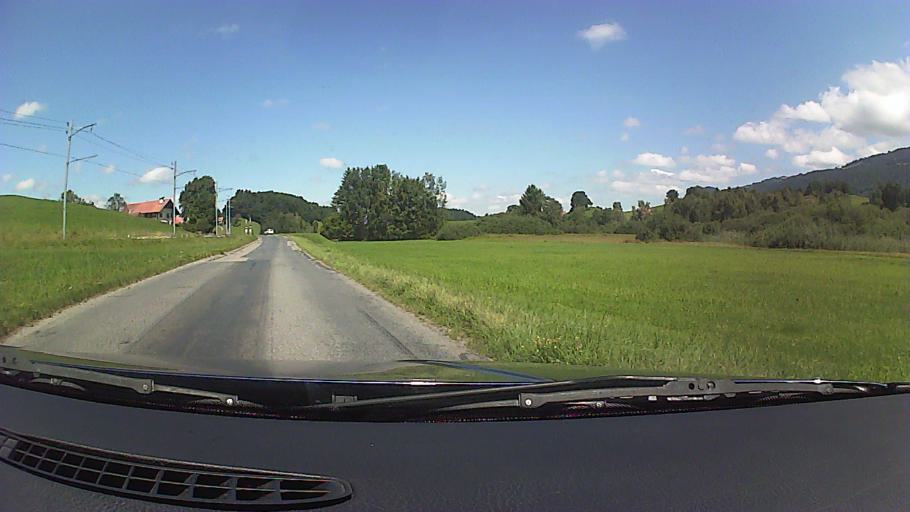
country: CH
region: Fribourg
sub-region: Veveyse District
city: Chatel-Saint-Denis
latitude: 46.5402
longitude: 6.8980
